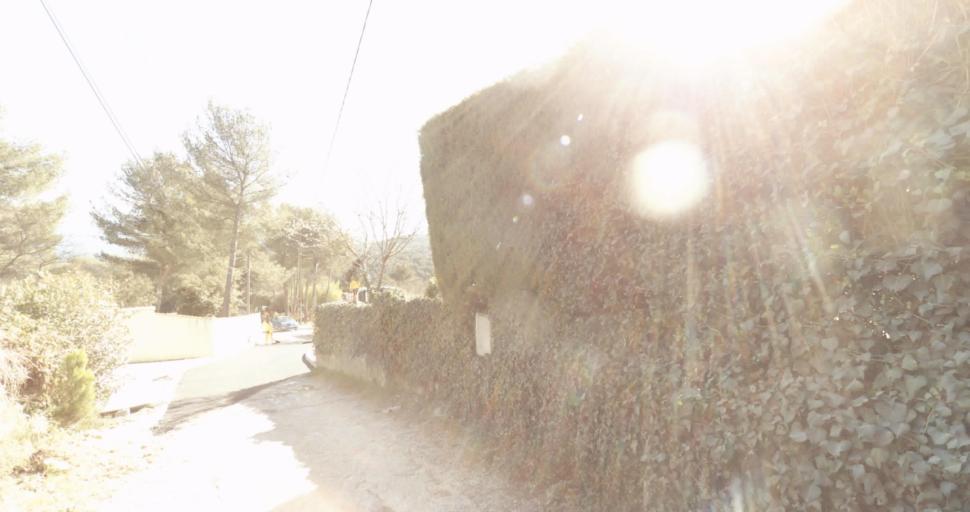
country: FR
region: Provence-Alpes-Cote d'Azur
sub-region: Departement des Bouches-du-Rhone
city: Peypin
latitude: 43.3879
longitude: 5.5704
